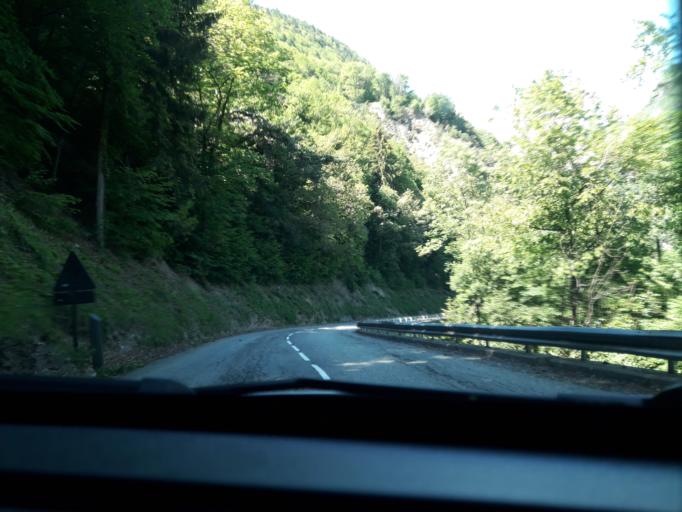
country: FR
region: Rhone-Alpes
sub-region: Departement de la Savoie
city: Salins-les-Thermes
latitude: 45.4764
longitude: 6.5244
